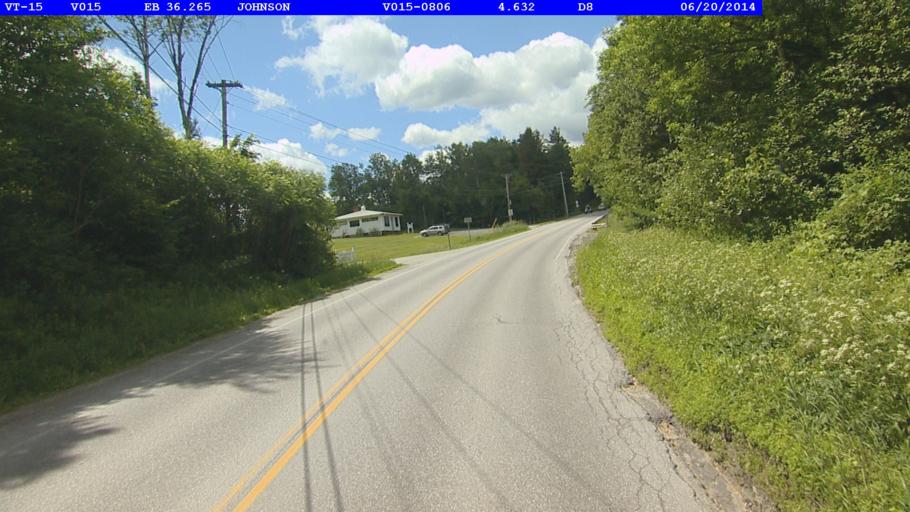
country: US
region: Vermont
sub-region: Lamoille County
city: Johnson
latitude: 44.6289
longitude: -72.6761
